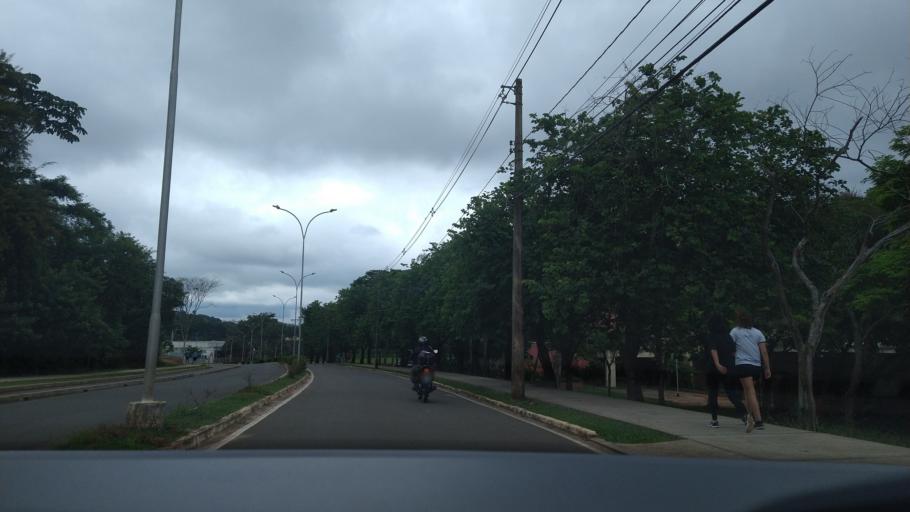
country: BR
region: Minas Gerais
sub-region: Vicosa
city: Vicosa
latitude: -20.7676
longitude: -42.8598
